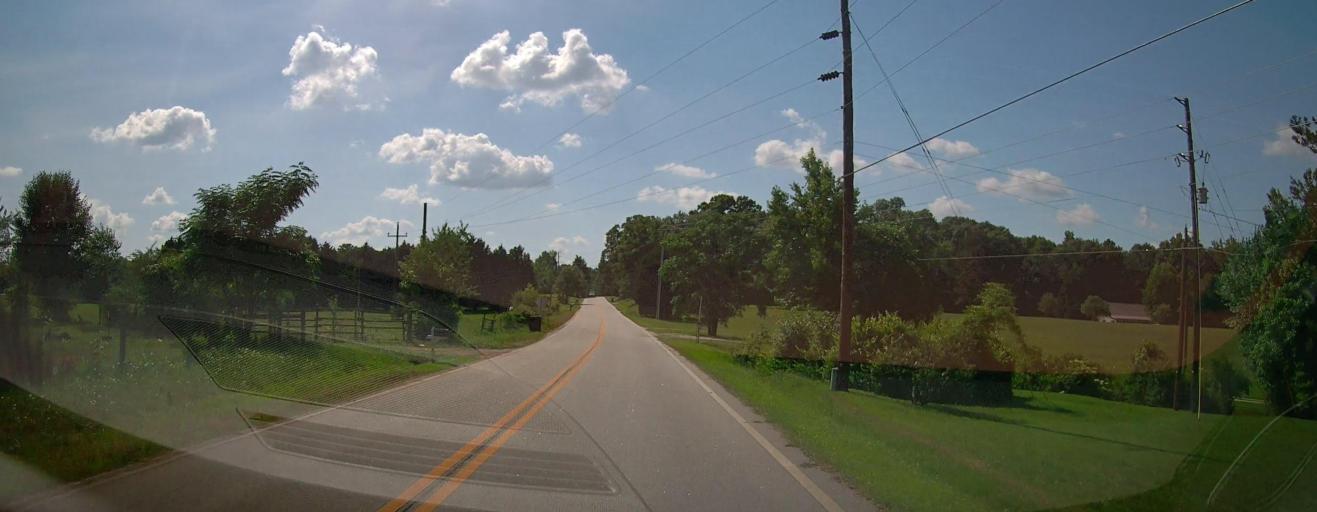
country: US
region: Georgia
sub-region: Spalding County
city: East Griffin
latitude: 33.2429
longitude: -84.1693
